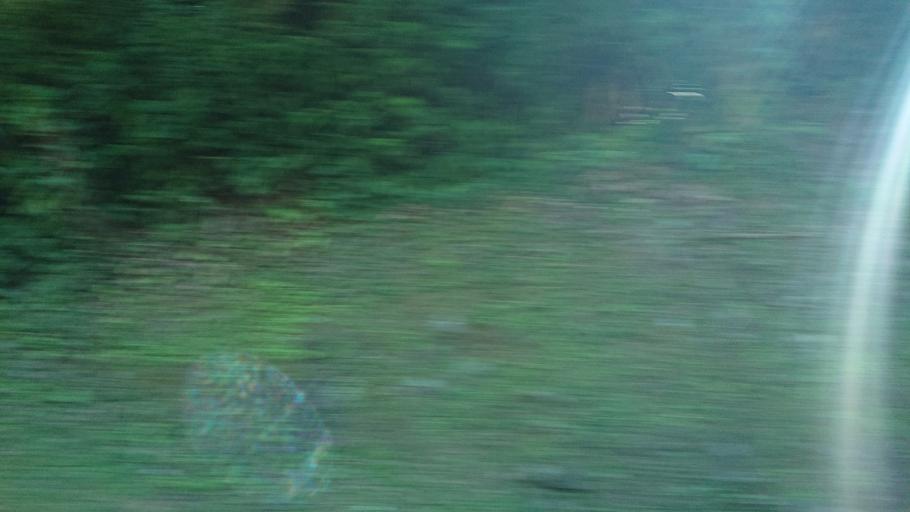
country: TW
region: Taiwan
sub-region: Yilan
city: Yilan
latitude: 24.5768
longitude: 121.4819
